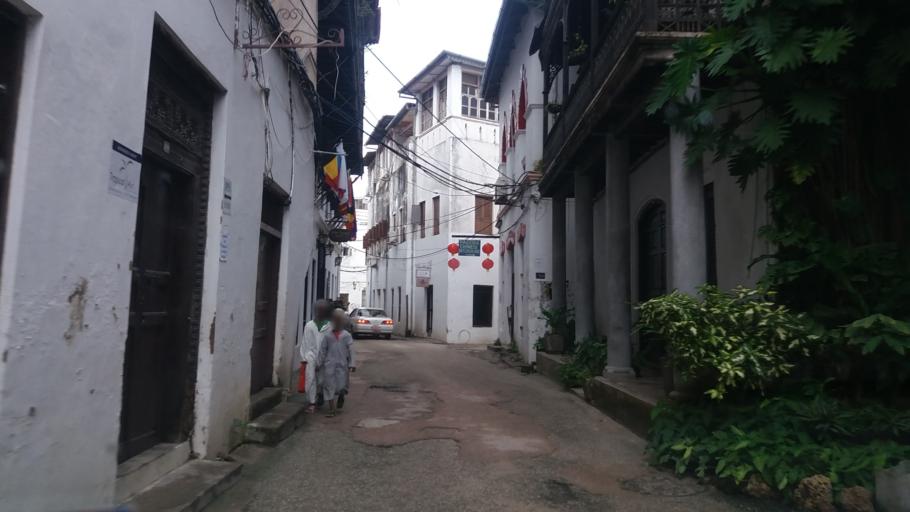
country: TZ
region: Zanzibar Urban/West
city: Zanzibar
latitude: -6.1640
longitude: 39.1875
